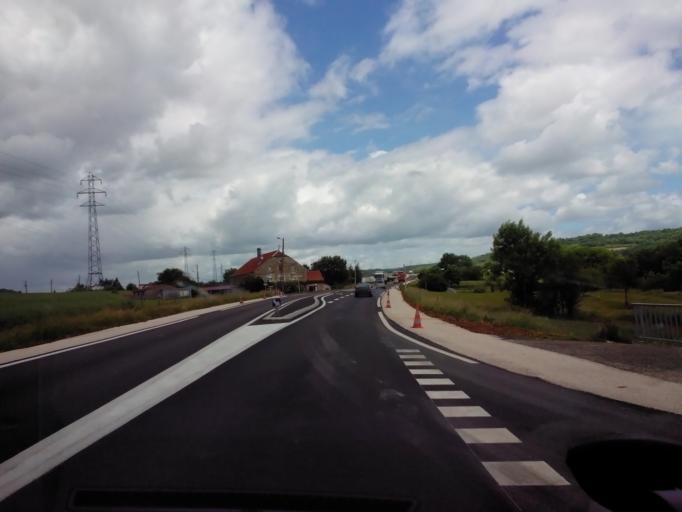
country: FR
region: Champagne-Ardenne
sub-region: Departement de la Haute-Marne
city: Rolampont
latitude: 47.9164
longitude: 5.2895
